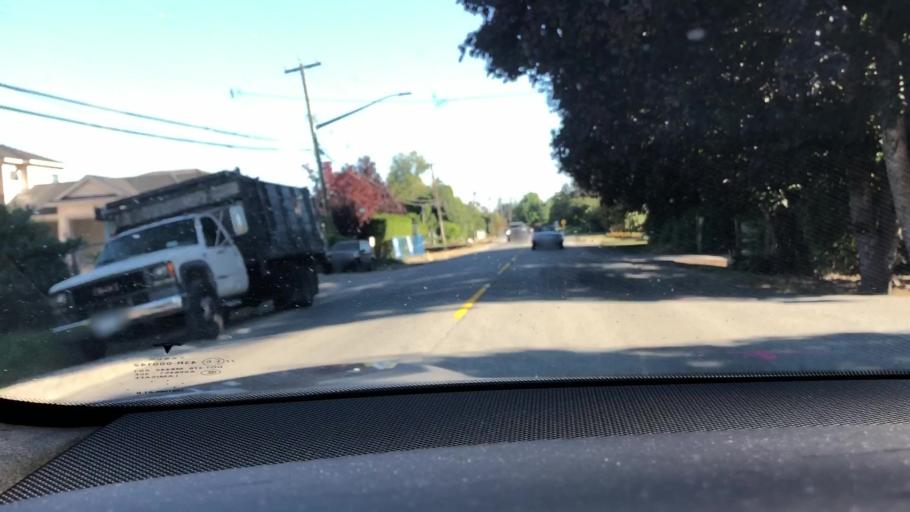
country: CA
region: British Columbia
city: Richmond
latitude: 49.1653
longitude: -123.0692
